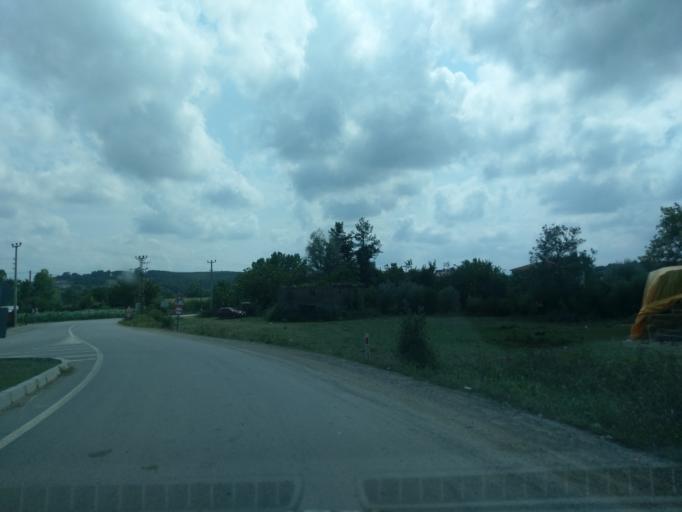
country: TR
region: Samsun
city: Bafra
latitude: 41.6005
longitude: 35.7624
